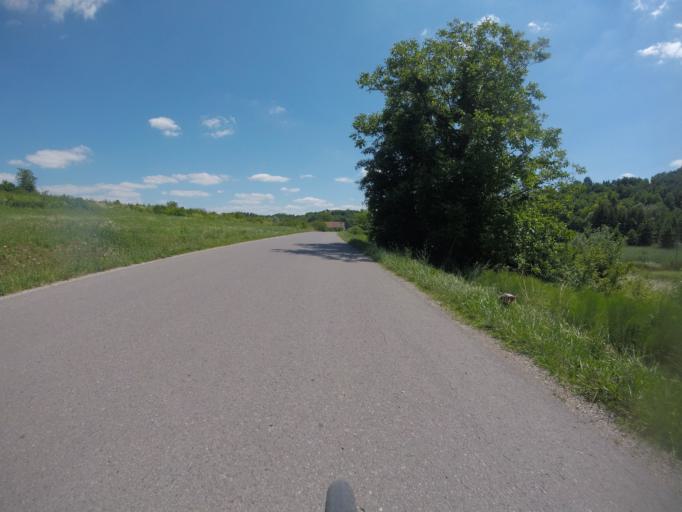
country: HR
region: Karlovacka
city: Ozalj
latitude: 45.6603
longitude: 15.4969
